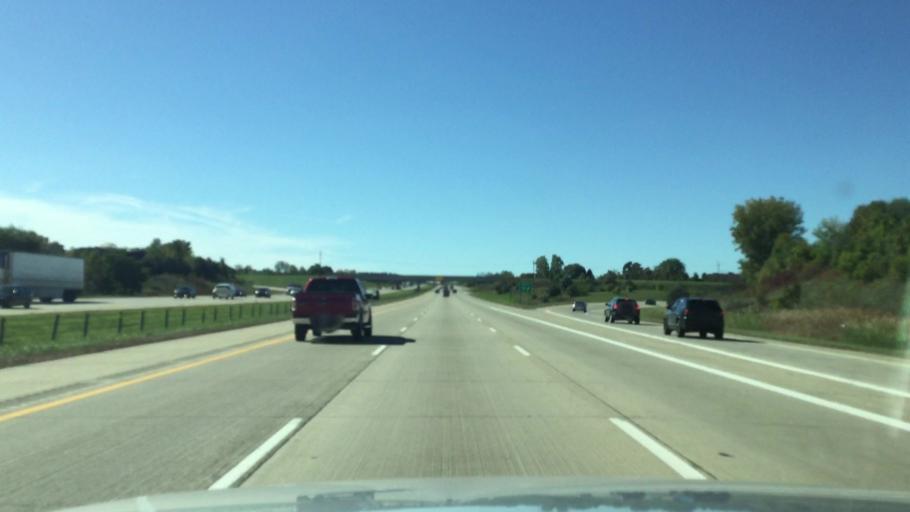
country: US
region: Michigan
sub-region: Wayne County
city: Plymouth
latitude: 42.3828
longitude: -83.5034
